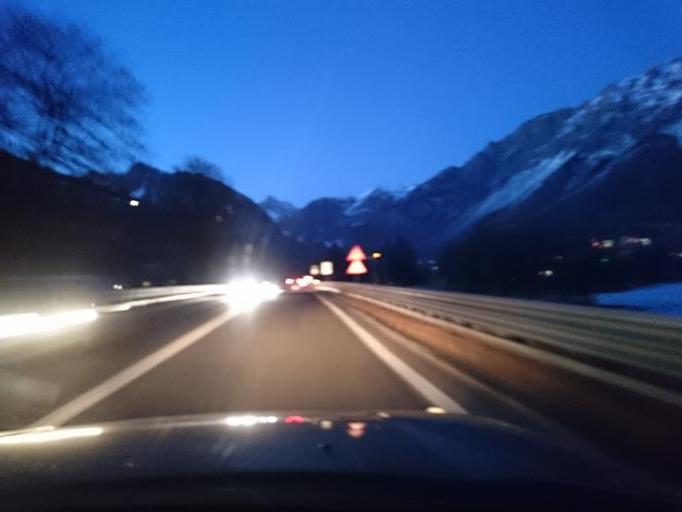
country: IT
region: Lombardy
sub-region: Provincia di Sondrio
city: Bormio
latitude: 46.4577
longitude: 10.3594
